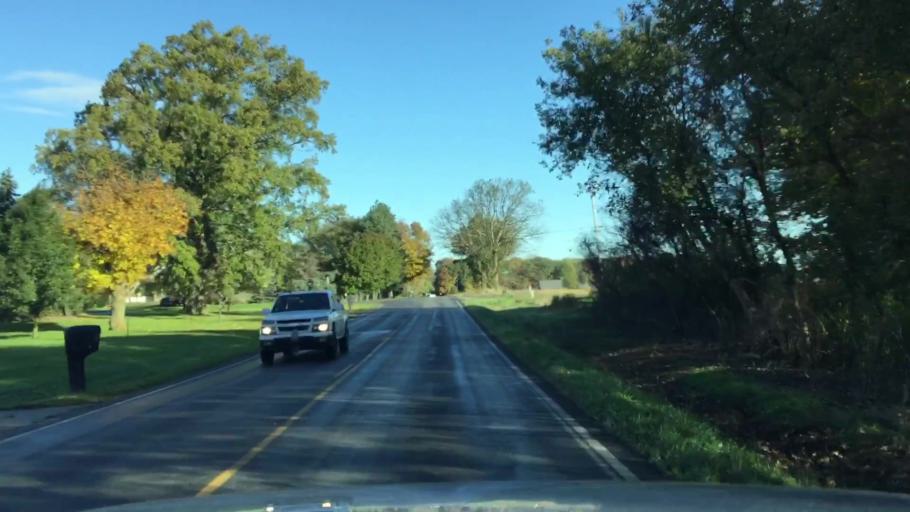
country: US
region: Michigan
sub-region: Shiawassee County
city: Durand
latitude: 42.9252
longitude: -83.9486
